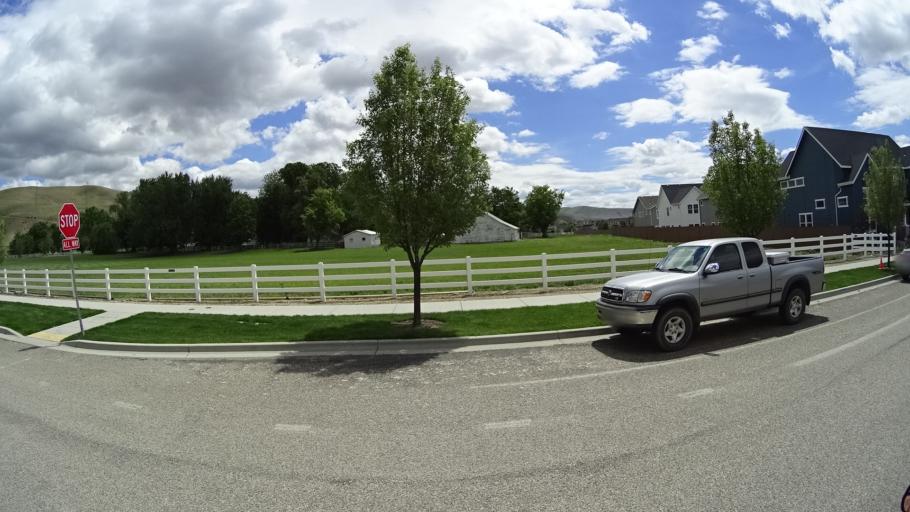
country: US
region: Idaho
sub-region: Ada County
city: Boise
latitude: 43.5772
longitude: -116.1320
